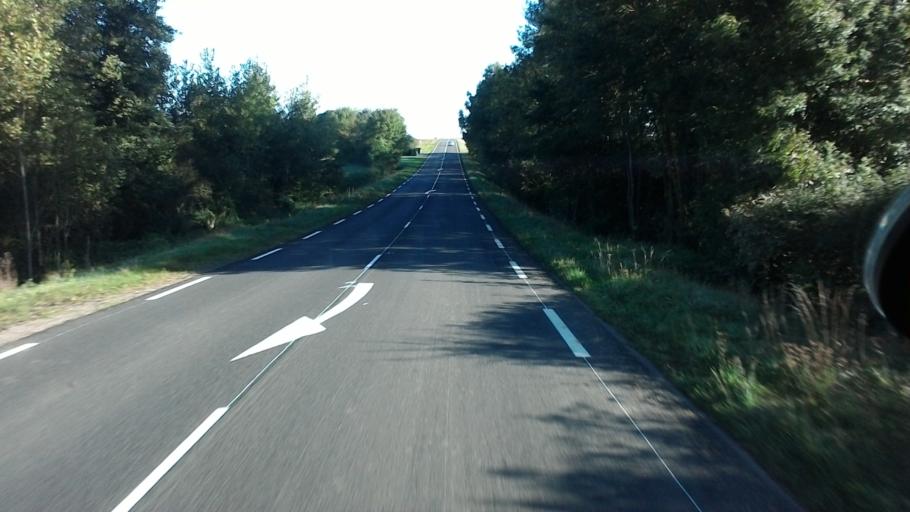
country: FR
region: Bourgogne
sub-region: Departement de la Cote-d'Or
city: Saulieu
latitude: 47.3714
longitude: 4.2913
